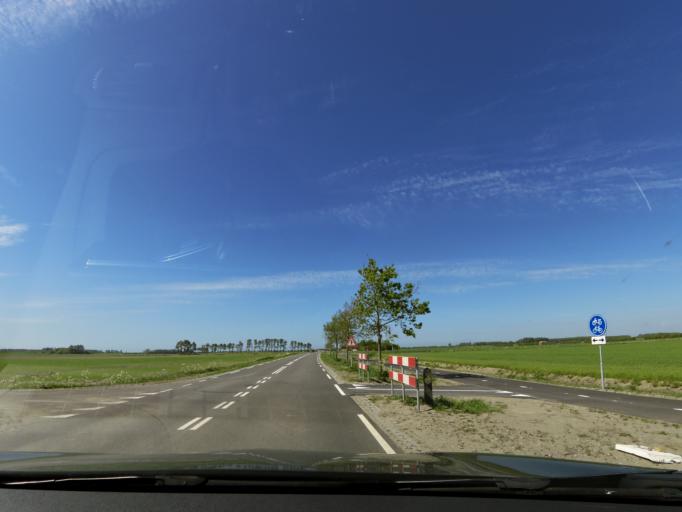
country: NL
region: Zeeland
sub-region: Schouwen-Duiveland
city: Bruinisse
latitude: 51.6612
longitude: 3.9900
